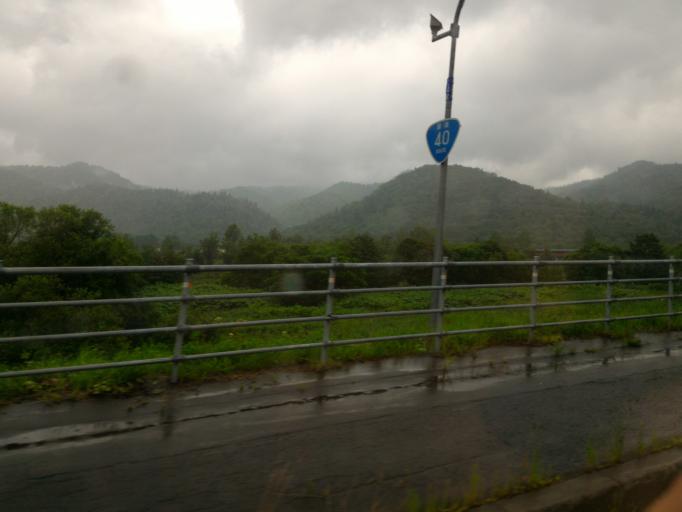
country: JP
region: Hokkaido
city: Nayoro
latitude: 44.7329
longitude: 142.1936
